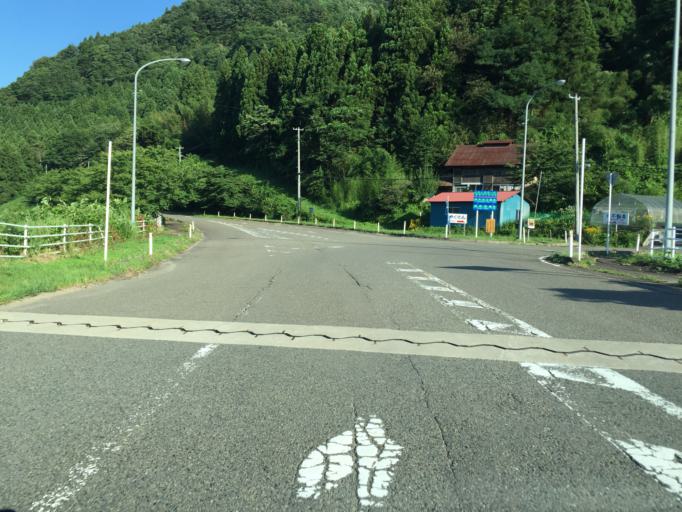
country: JP
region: Miyagi
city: Shiroishi
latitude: 37.9439
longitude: 140.5418
